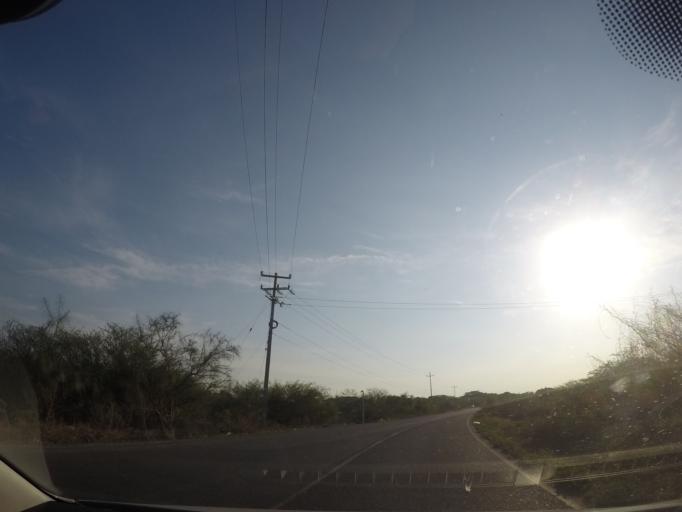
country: MX
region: Oaxaca
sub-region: Santo Domingo Tehuantepec
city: La Noria
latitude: 16.2297
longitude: -95.1849
